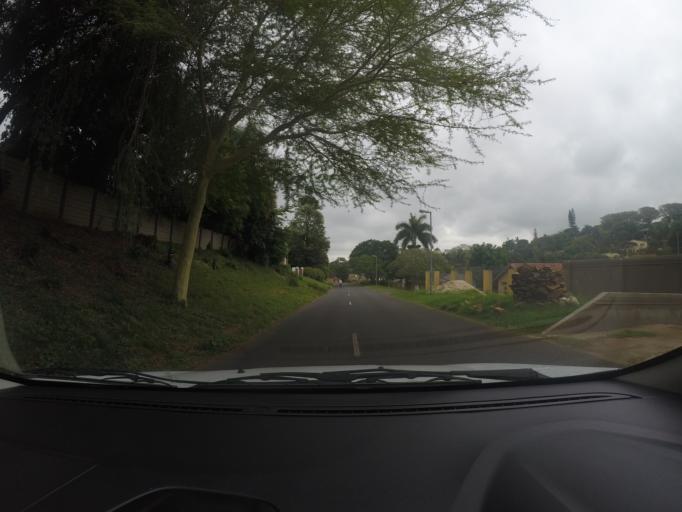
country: ZA
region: KwaZulu-Natal
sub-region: uThungulu District Municipality
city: Empangeni
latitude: -28.7612
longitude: 31.8906
